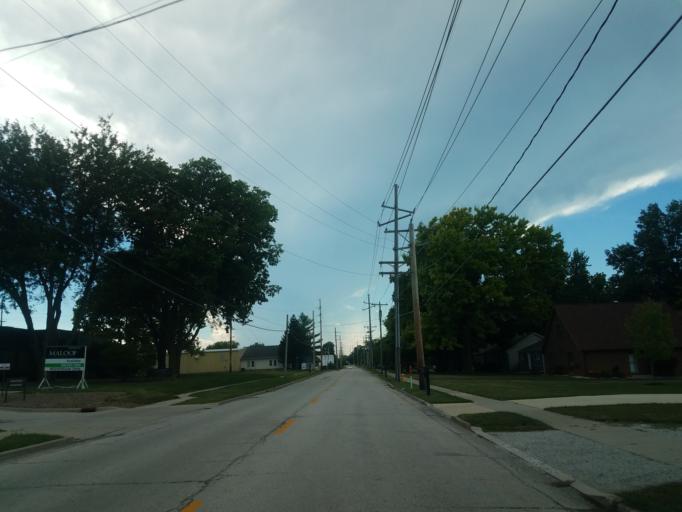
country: US
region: Illinois
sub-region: McLean County
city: Bloomington
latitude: 40.4636
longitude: -88.9779
